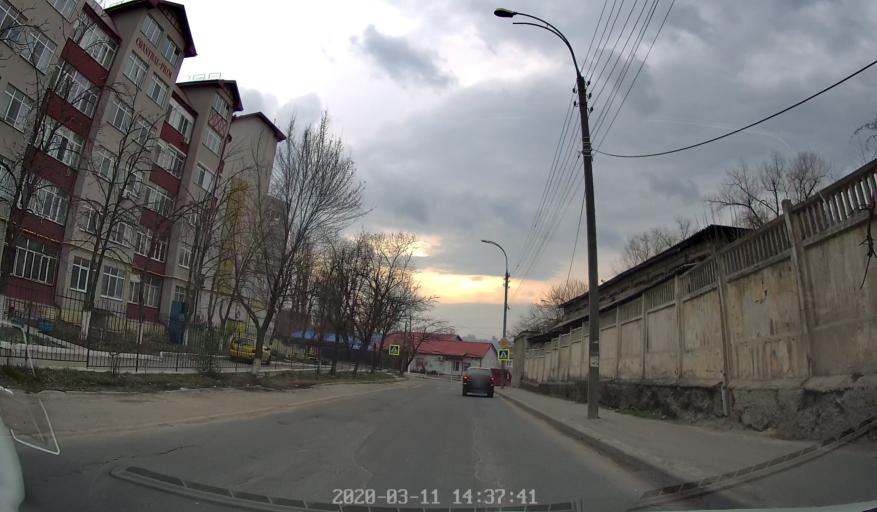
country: MD
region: Chisinau
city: Chisinau
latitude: 47.0206
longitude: 28.8744
